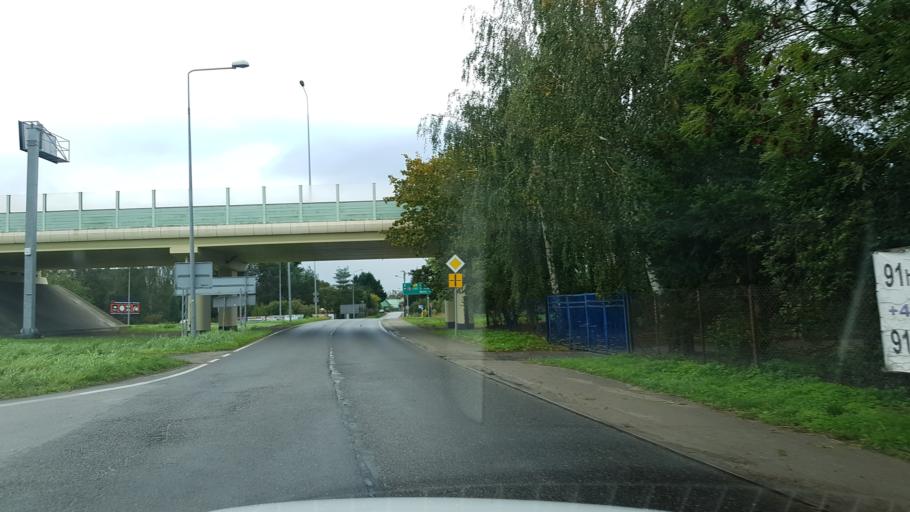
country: PL
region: West Pomeranian Voivodeship
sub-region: Powiat kamienski
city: Wolin
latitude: 53.8453
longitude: 14.6289
